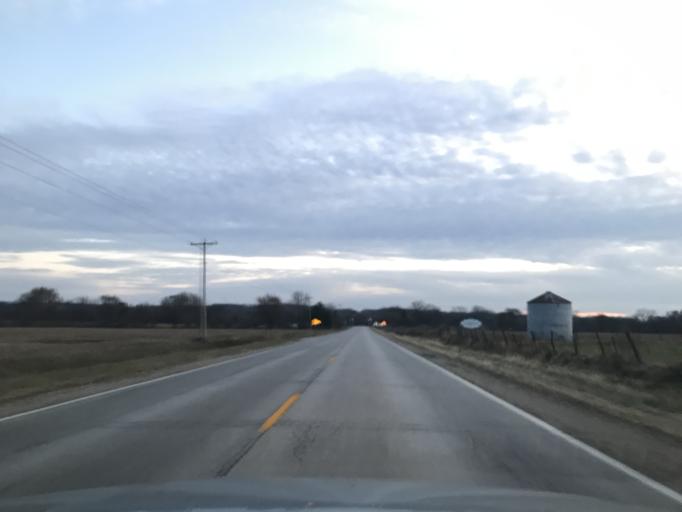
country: US
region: Iowa
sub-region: Des Moines County
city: Burlington
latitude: 40.6880
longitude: -91.0703
